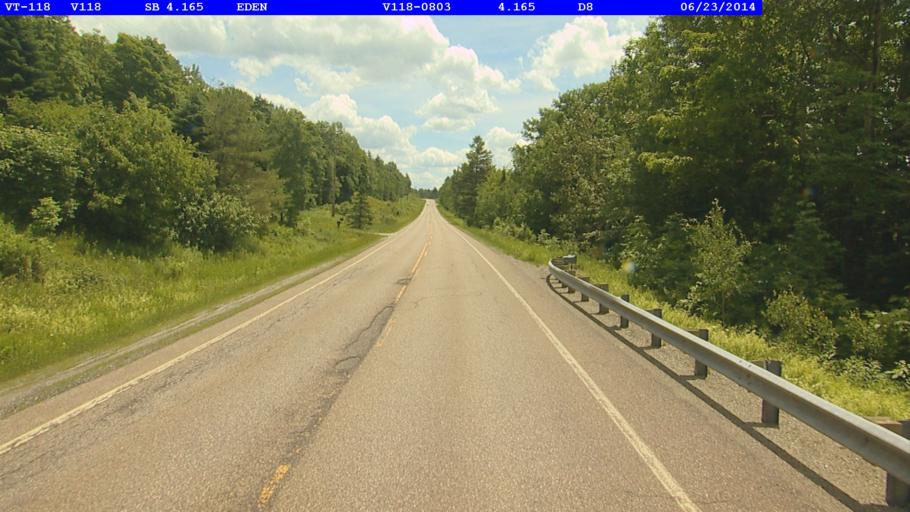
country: US
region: Vermont
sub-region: Lamoille County
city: Johnson
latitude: 44.7586
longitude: -72.5831
